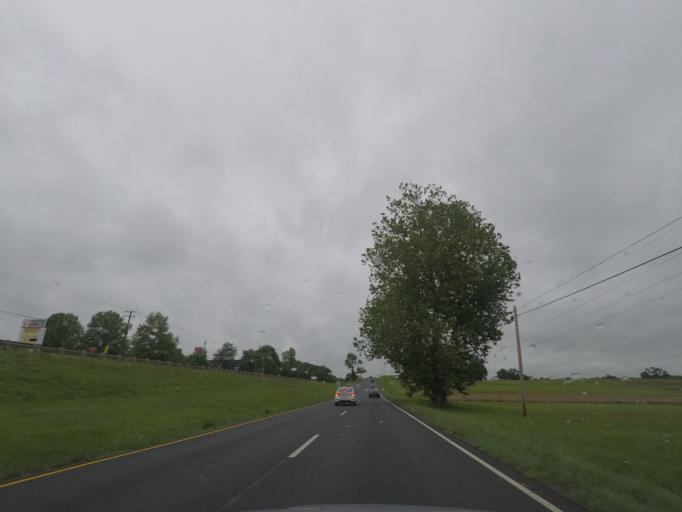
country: US
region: Virginia
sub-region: Orange County
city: Orange
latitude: 38.2227
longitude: -78.1233
